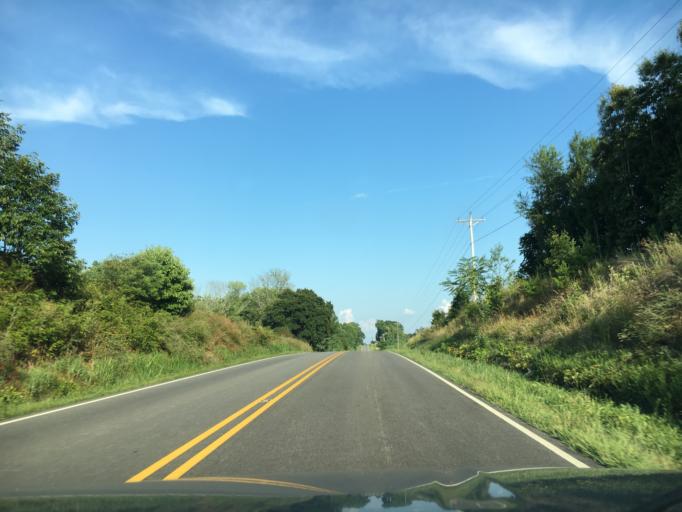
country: US
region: Virginia
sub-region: Franklin County
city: Union Hall
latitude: 36.9611
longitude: -79.5742
